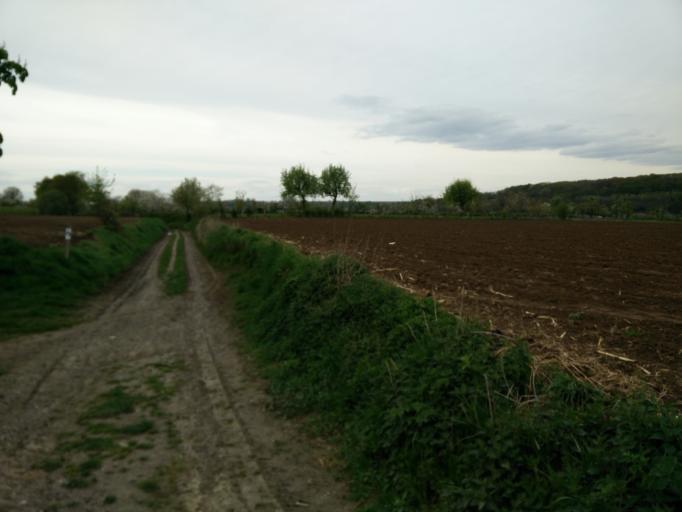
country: BE
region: Flanders
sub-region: Provincie Limburg
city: Sint-Pieters-Voeren
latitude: 50.7513
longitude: 5.7707
